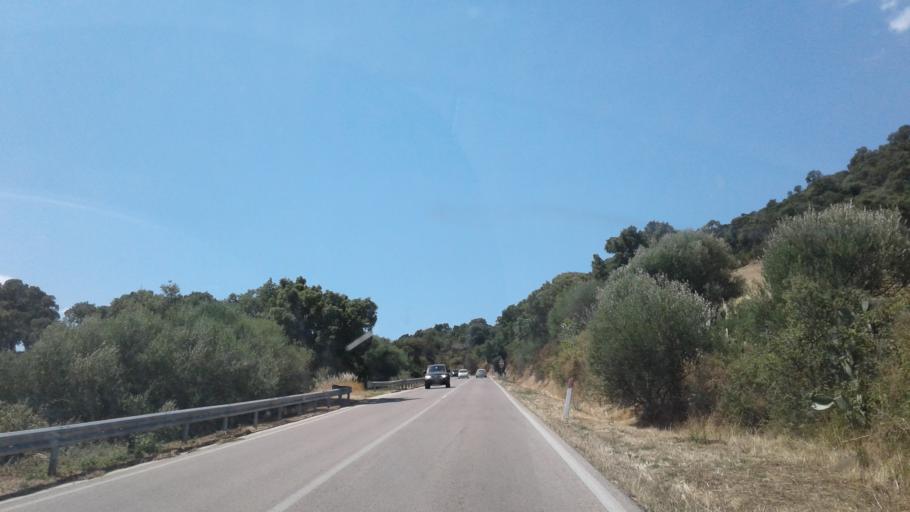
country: IT
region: Sardinia
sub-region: Provincia di Olbia-Tempio
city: Luras
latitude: 40.9533
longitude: 9.2038
